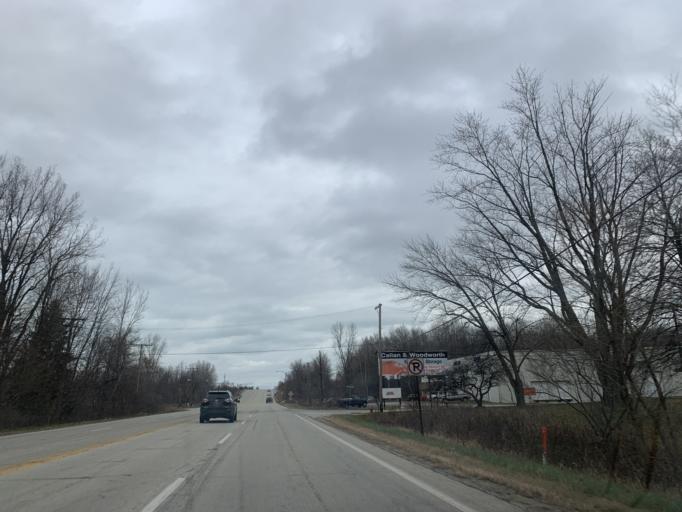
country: US
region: Indiana
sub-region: LaPorte County
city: Trail Creek
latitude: 41.7113
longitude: -86.8259
